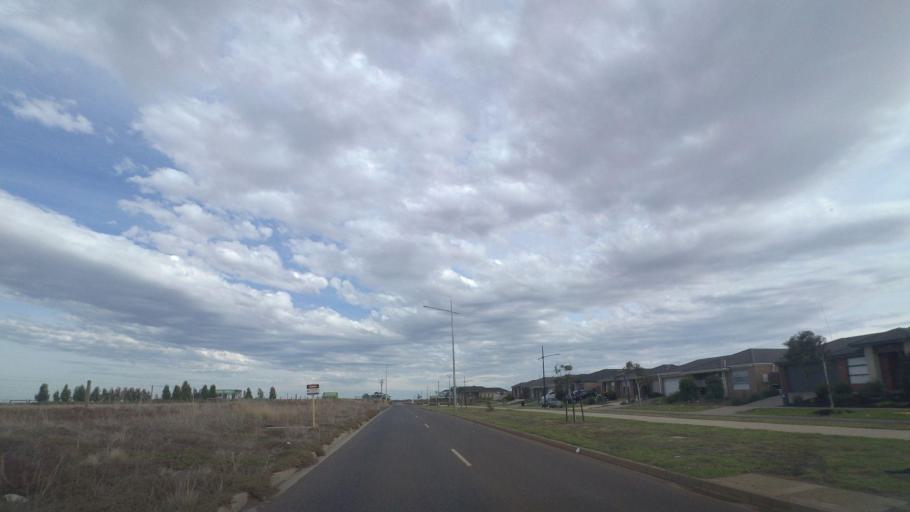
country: AU
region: Victoria
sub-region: Melton
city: Melton South
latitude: -37.7174
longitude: 144.5620
